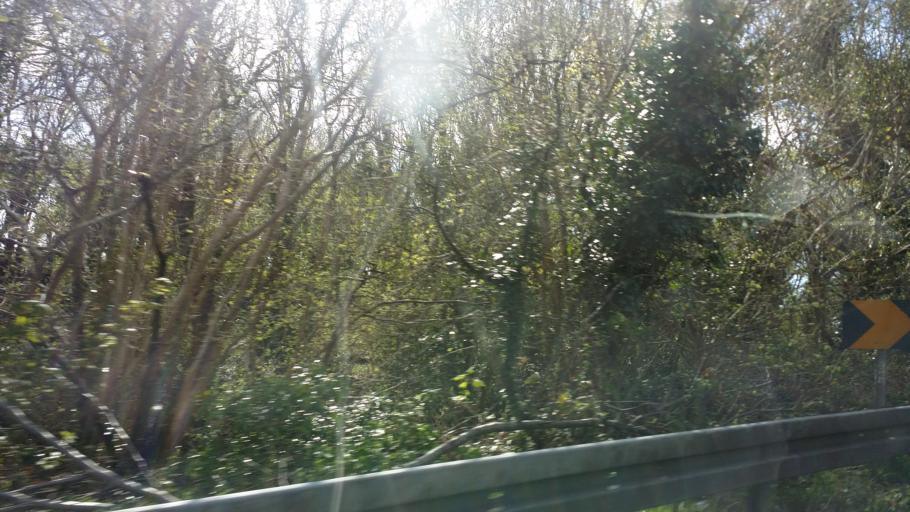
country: IE
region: Ulster
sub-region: County Donegal
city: Ballyshannon
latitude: 54.4869
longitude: -8.1377
